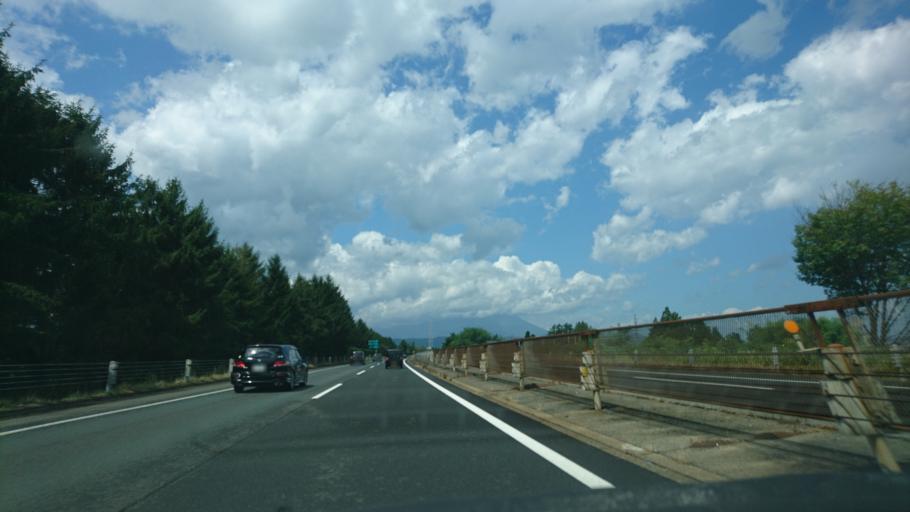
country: JP
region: Iwate
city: Morioka-shi
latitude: 39.6690
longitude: 141.1089
